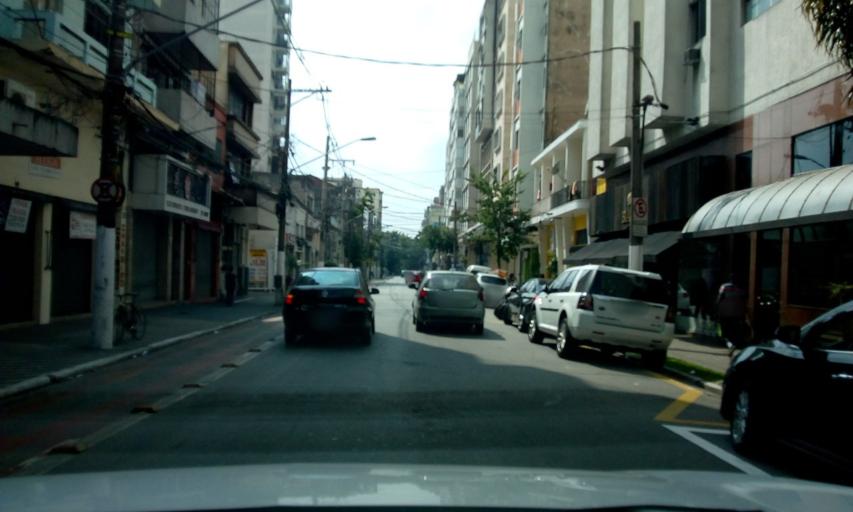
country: BR
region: Sao Paulo
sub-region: Sao Paulo
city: Sao Paulo
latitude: -23.5315
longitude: -46.6366
